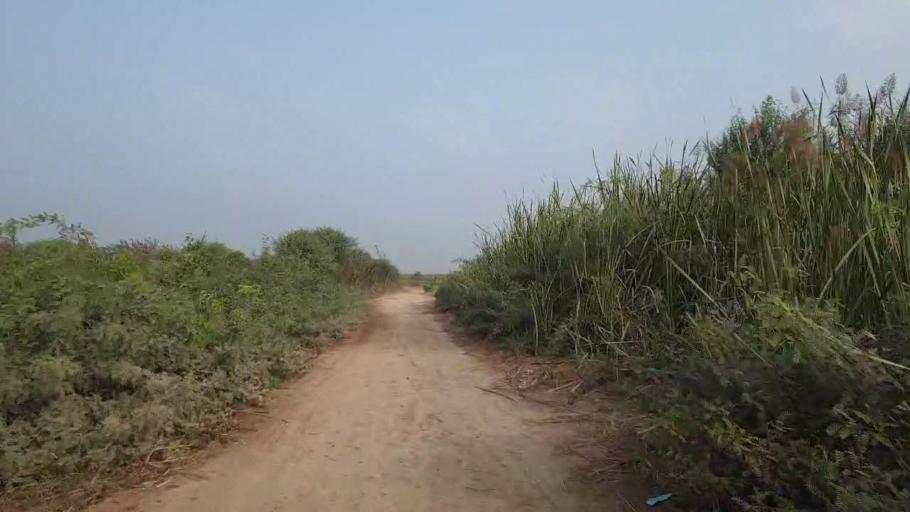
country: PK
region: Sindh
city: Tando Muhammad Khan
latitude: 25.1430
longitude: 68.5910
